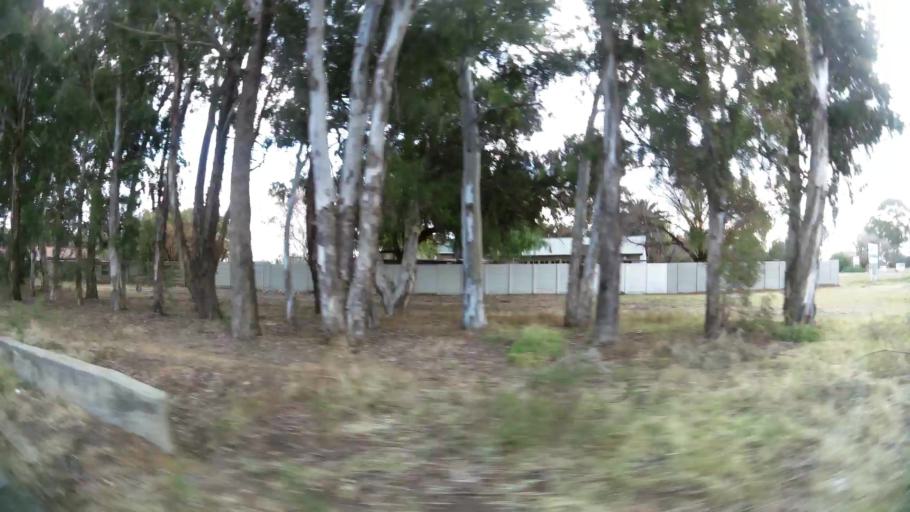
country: ZA
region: Orange Free State
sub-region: Lejweleputswa District Municipality
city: Welkom
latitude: -27.9946
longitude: 26.7091
